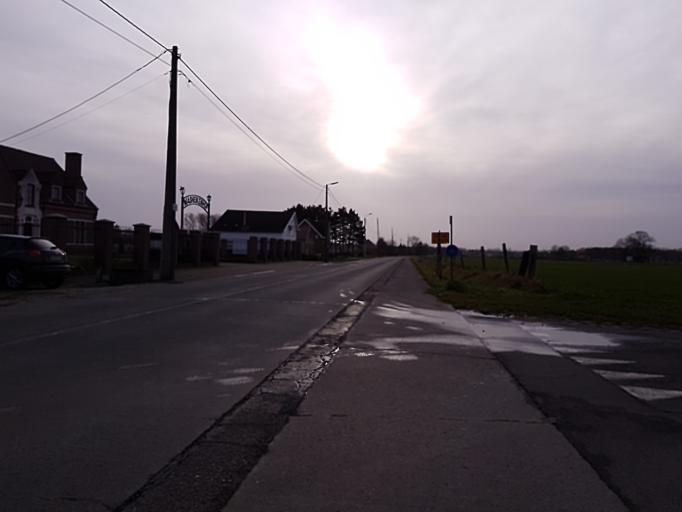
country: BE
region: Flanders
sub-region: Provincie Antwerpen
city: Putte
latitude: 51.0445
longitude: 4.6803
